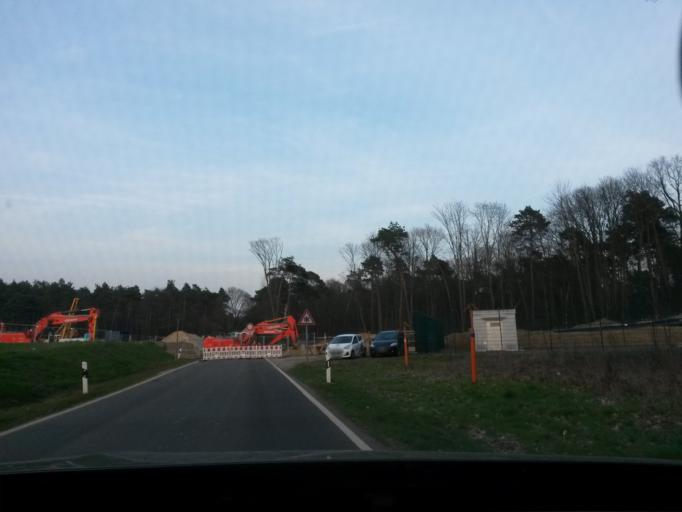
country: DE
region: Brandenburg
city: Protzel
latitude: 52.5966
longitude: 13.9707
